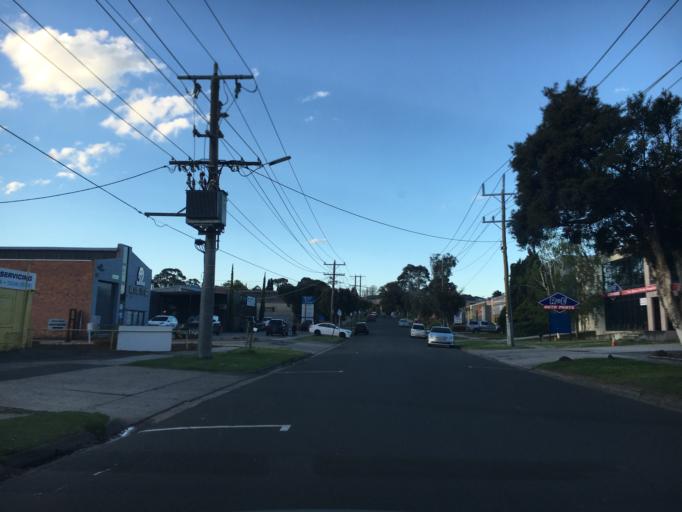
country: AU
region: Victoria
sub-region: Monash
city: Notting Hill
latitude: -37.8864
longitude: 145.1580
